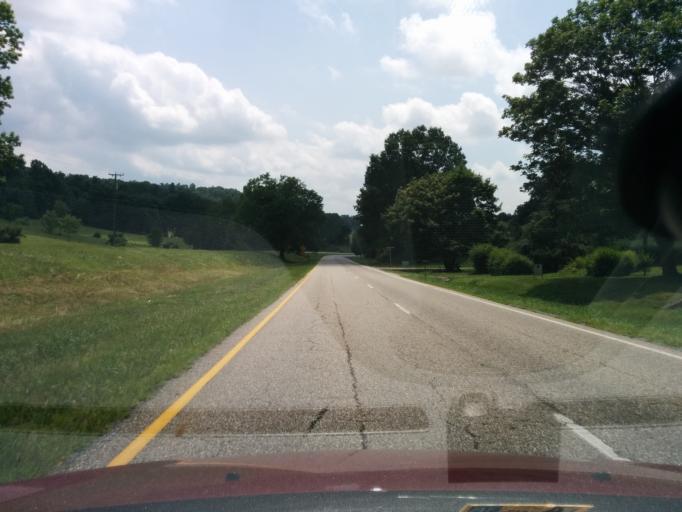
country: US
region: Virginia
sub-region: Rockbridge County
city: East Lexington
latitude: 37.8517
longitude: -79.3362
